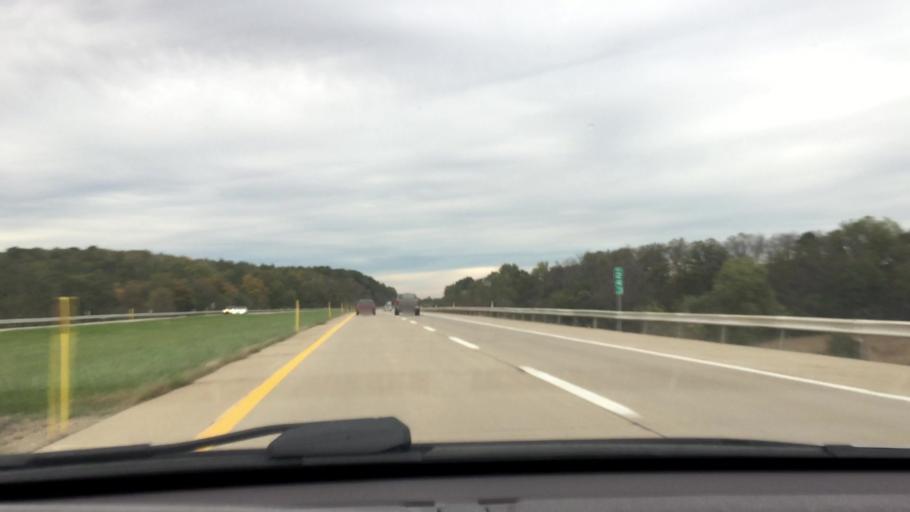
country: US
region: Pennsylvania
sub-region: Lawrence County
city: New Beaver
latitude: 40.8580
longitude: -80.3687
